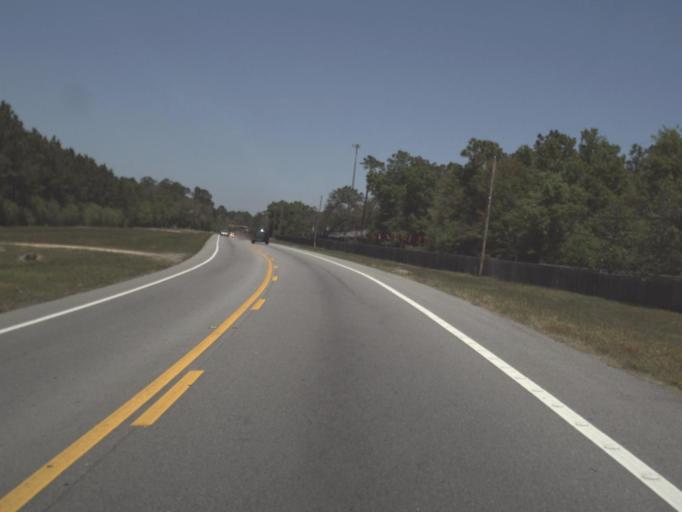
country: US
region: Florida
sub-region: Escambia County
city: Myrtle Grove
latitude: 30.4282
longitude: -87.3252
